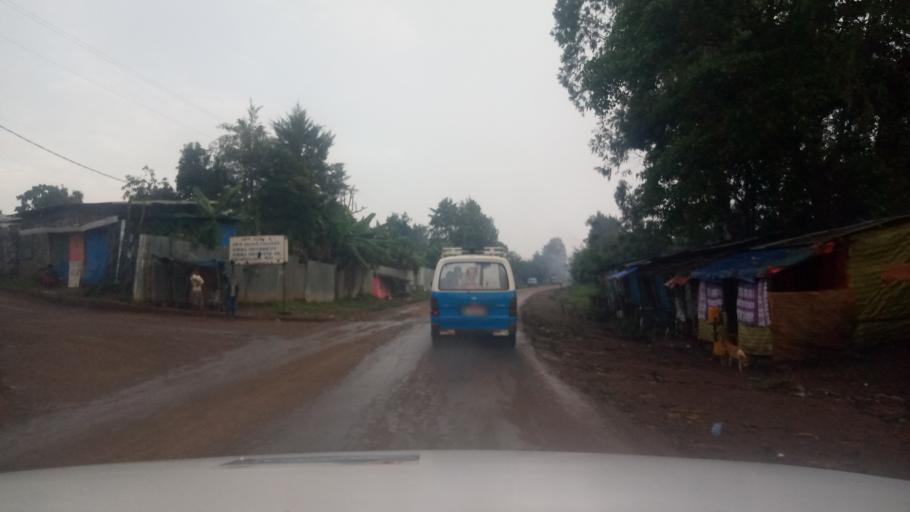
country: ET
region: Oromiya
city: Jima
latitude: 7.6951
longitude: 36.8176
